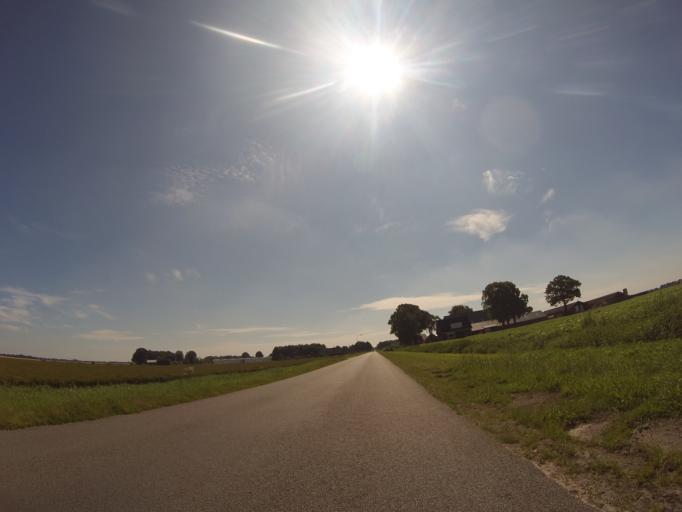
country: NL
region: Drenthe
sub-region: Gemeente Emmen
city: Schoonebeek
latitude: 52.6975
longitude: 6.9272
